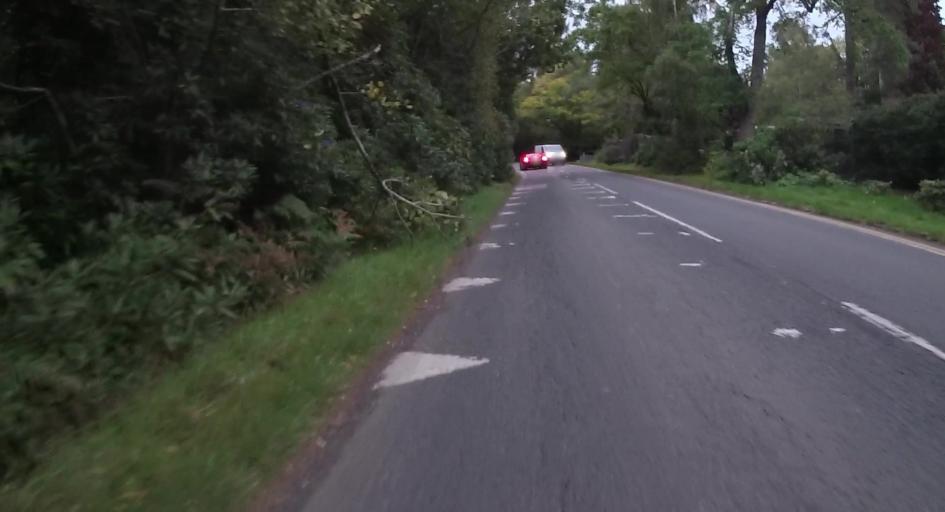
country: GB
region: England
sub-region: Wokingham
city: Finchampstead
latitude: 51.3667
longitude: -0.8426
